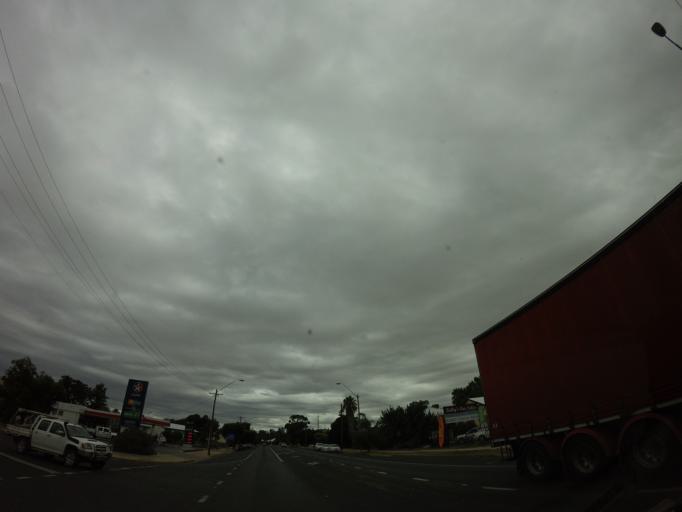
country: AU
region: New South Wales
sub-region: Narrabri
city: Narrabri
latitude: -30.3305
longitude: 149.7756
